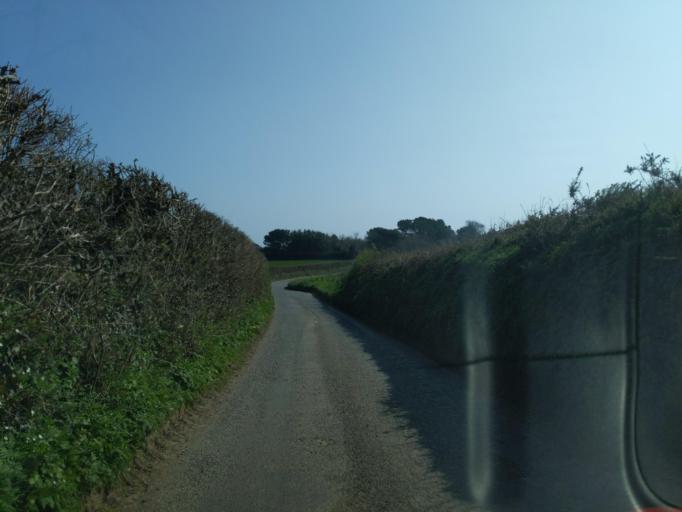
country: GB
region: England
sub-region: Devon
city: Dartmouth
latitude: 50.3169
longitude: -3.6332
